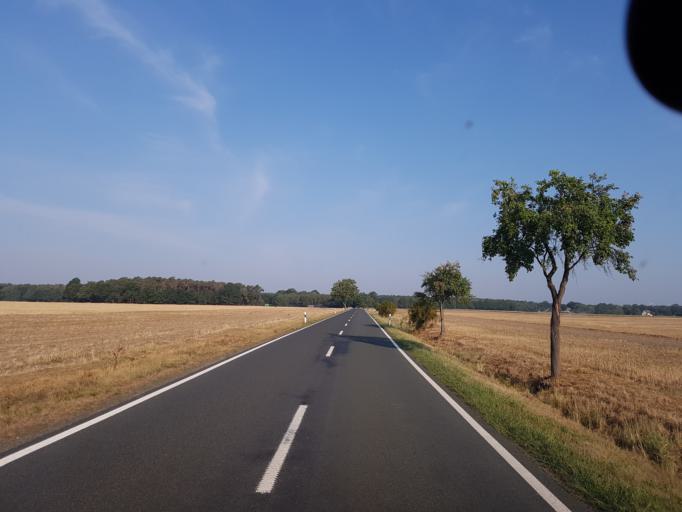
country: DE
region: Brandenburg
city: Finsterwalde
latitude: 51.6748
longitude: 13.7021
